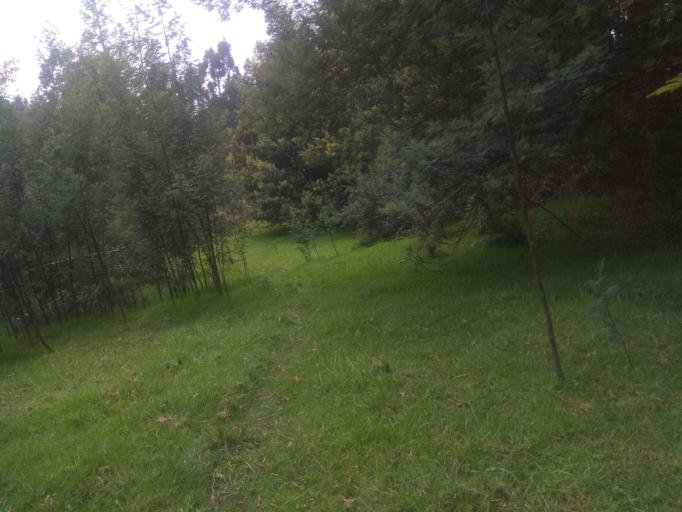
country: CO
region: Boyaca
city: Socota
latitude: 6.0179
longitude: -72.6595
